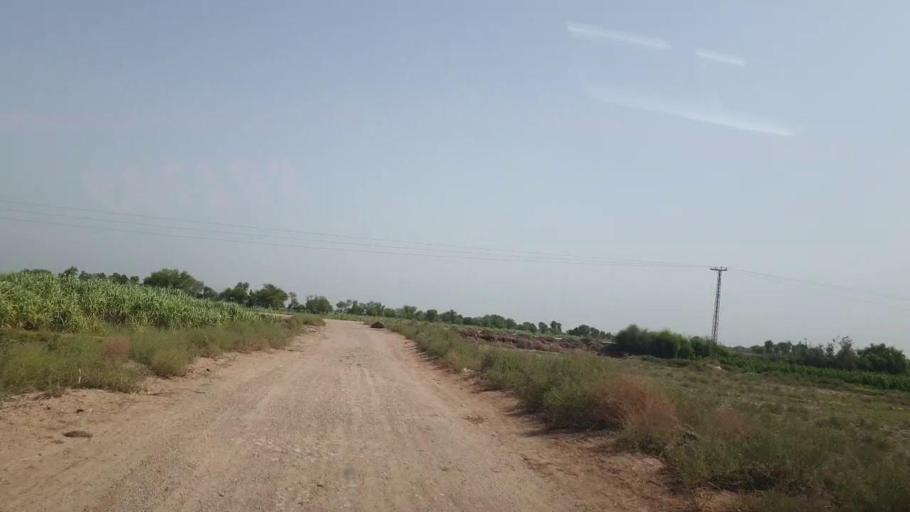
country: PK
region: Sindh
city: Daur
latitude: 26.3186
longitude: 68.2154
